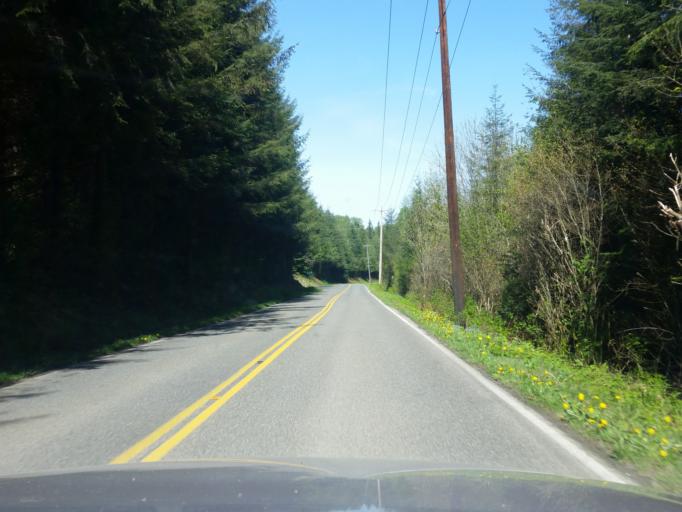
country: US
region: Washington
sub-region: Snohomish County
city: Granite Falls
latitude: 48.0094
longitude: -121.9143
